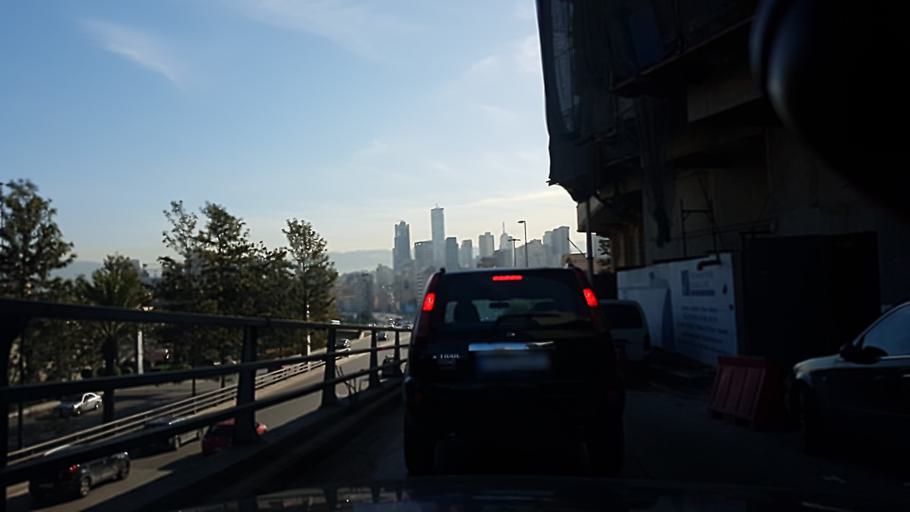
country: LB
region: Beyrouth
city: Beirut
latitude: 33.8940
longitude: 35.4997
